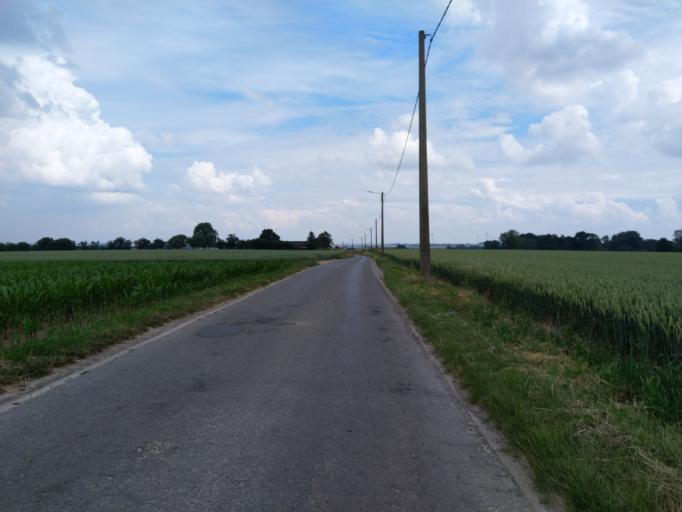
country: FR
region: Nord-Pas-de-Calais
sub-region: Departement du Nord
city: Boussois
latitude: 50.3626
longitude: 4.0266
